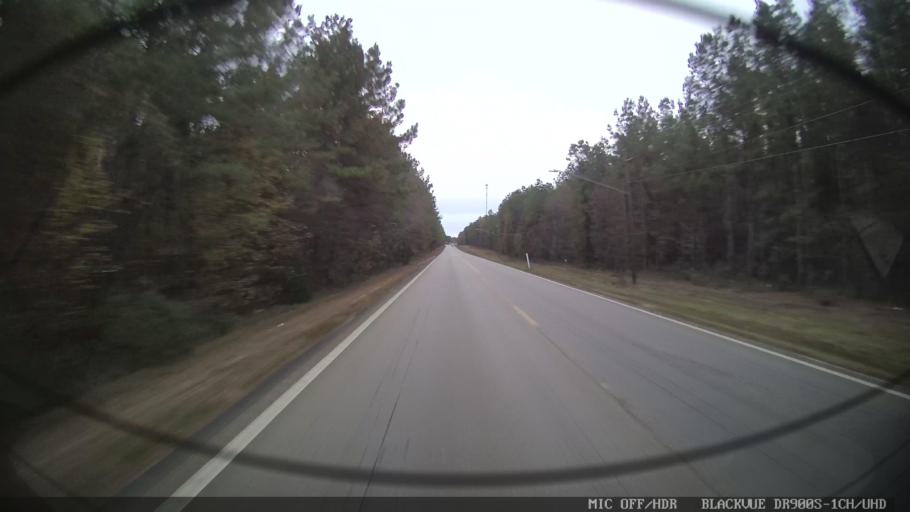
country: US
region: Mississippi
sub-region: Clarke County
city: Stonewall
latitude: 32.0504
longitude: -88.8956
